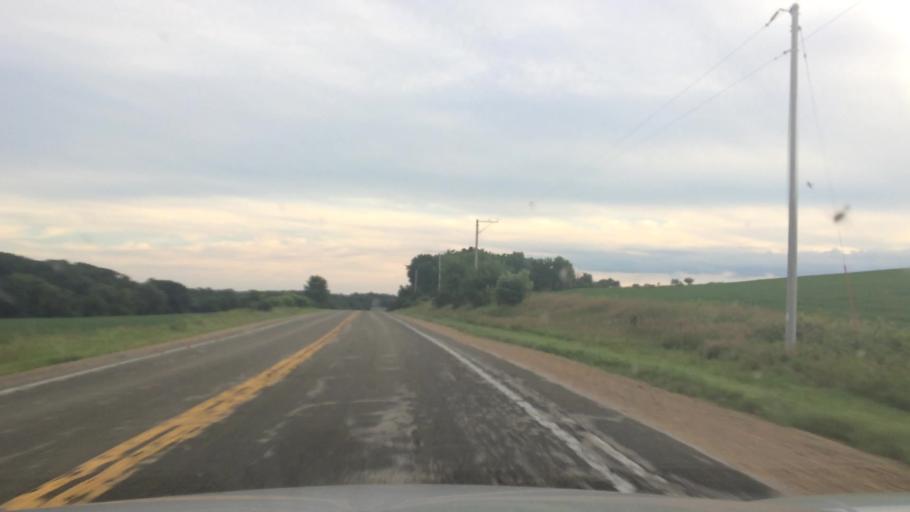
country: US
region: Wisconsin
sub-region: Columbia County
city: Lodi
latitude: 43.3298
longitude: -89.4837
